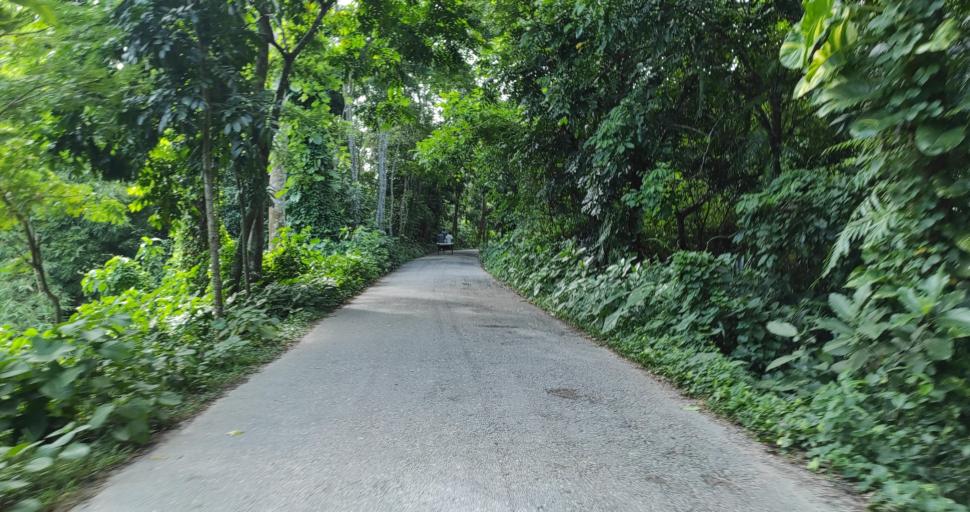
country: BD
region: Barisal
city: Gaurnadi
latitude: 22.8939
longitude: 90.1863
